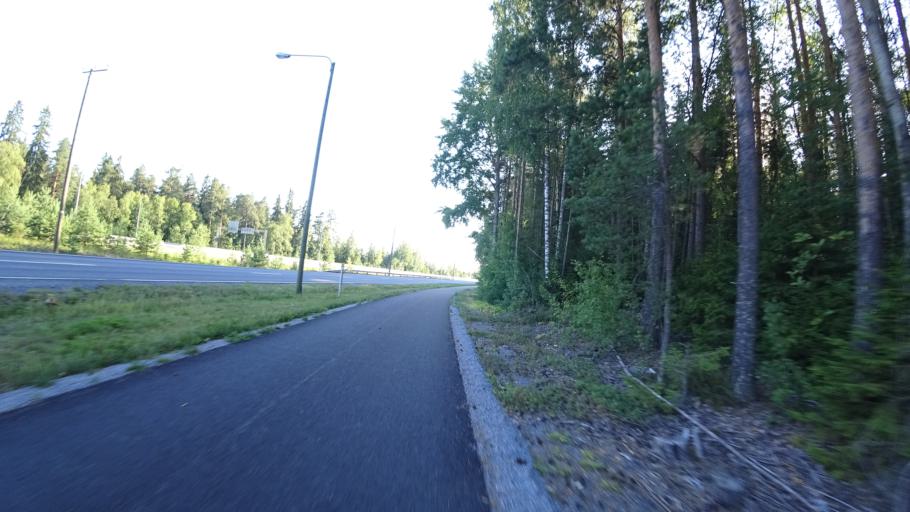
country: FI
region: Pirkanmaa
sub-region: Tampere
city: Pirkkala
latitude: 61.4856
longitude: 23.5750
